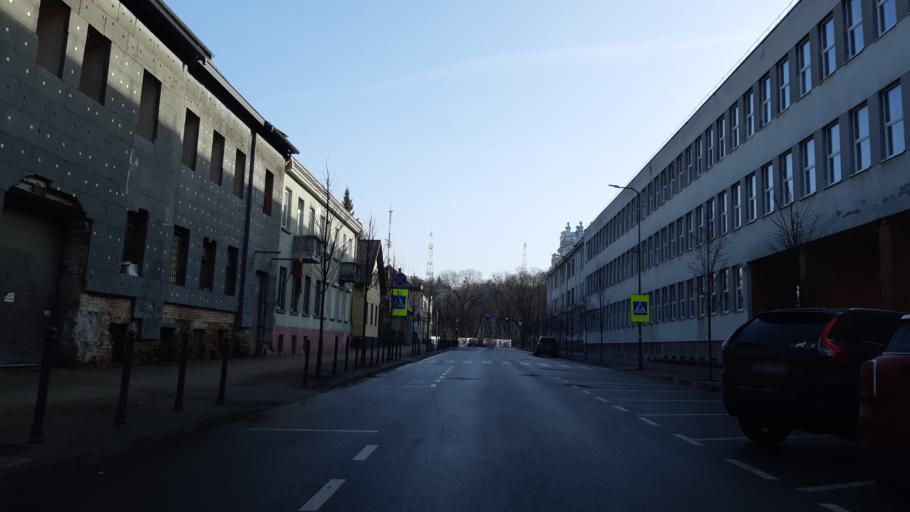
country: LT
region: Kauno apskritis
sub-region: Kaunas
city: Kaunas
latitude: 54.8937
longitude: 23.9224
